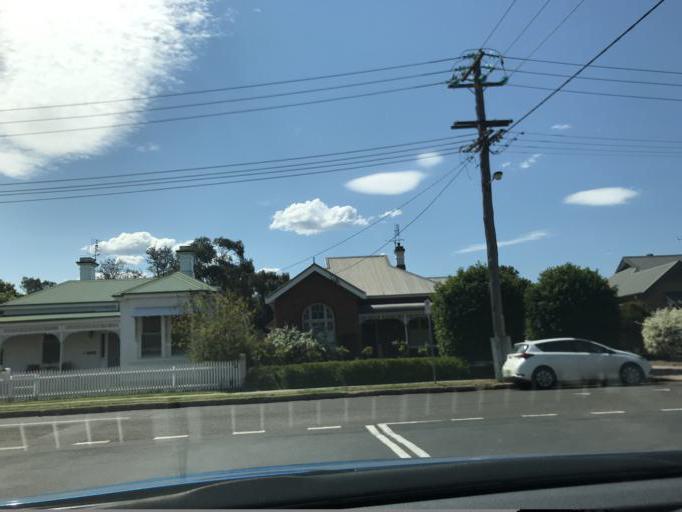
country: AU
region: New South Wales
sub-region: Singleton
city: Singleton
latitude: -32.5639
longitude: 151.1729
